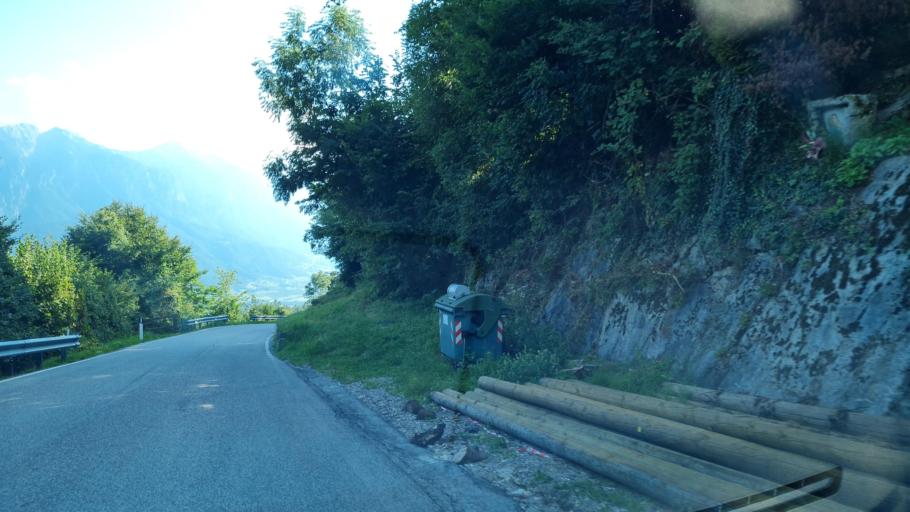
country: IT
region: Trentino-Alto Adige
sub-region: Provincia di Trento
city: Samone
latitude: 46.0965
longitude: 11.5008
